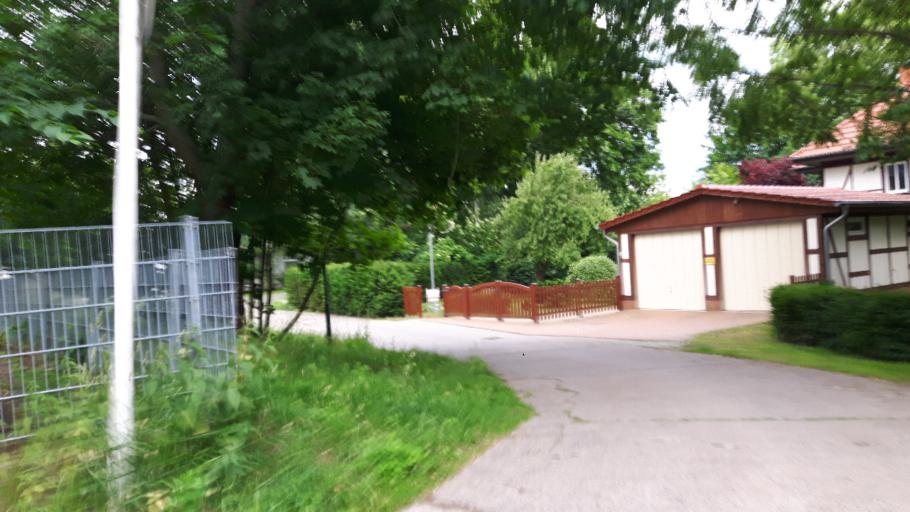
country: DE
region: Brandenburg
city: Schwedt (Oder)
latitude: 53.0564
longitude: 14.2943
